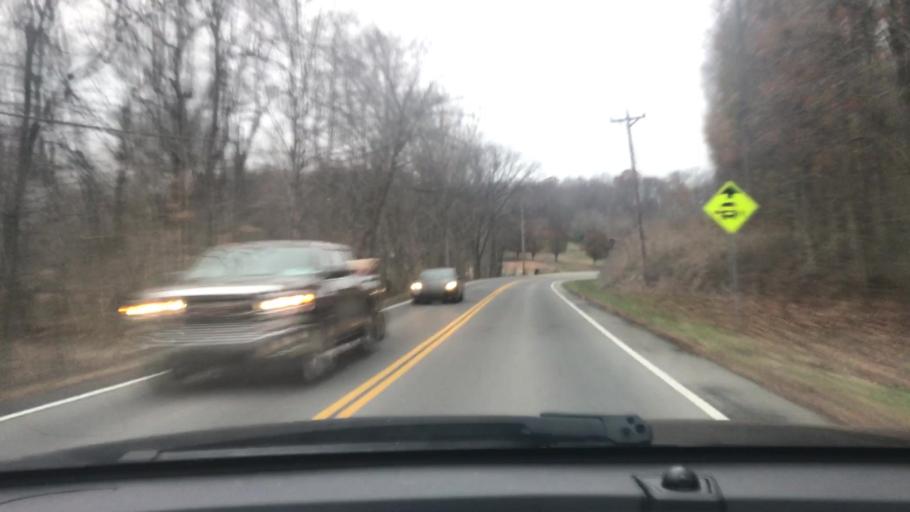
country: US
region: Tennessee
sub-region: Dickson County
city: Charlotte
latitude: 36.2426
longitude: -87.3470
